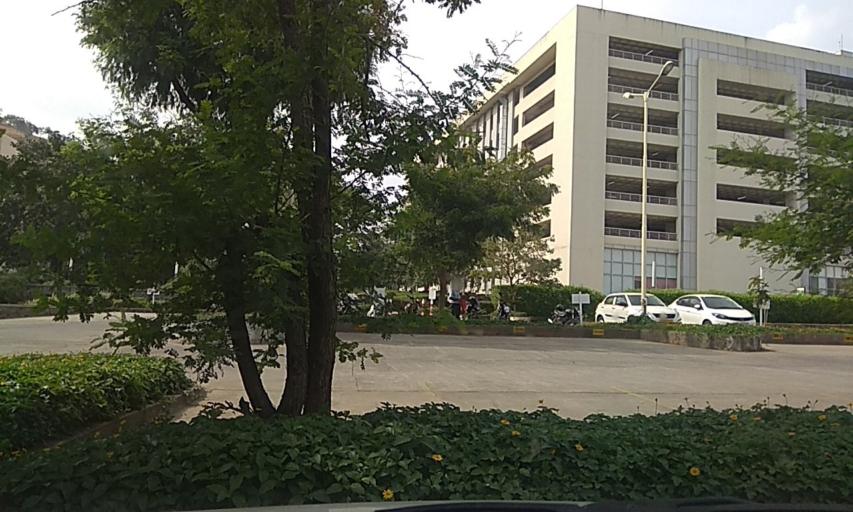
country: IN
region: Maharashtra
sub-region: Pune Division
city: Pimpri
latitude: 18.6043
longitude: 73.7165
